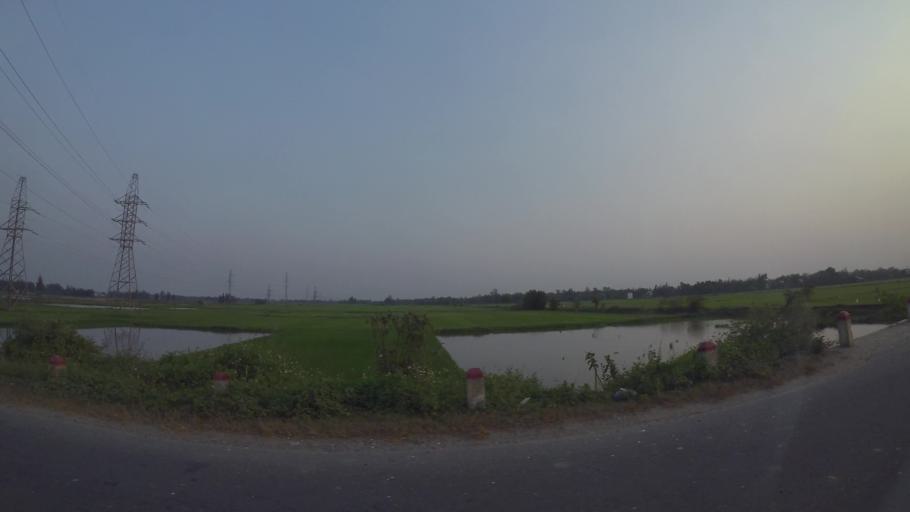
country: VN
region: Da Nang
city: Ngu Hanh Son
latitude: 15.9533
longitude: 108.2368
